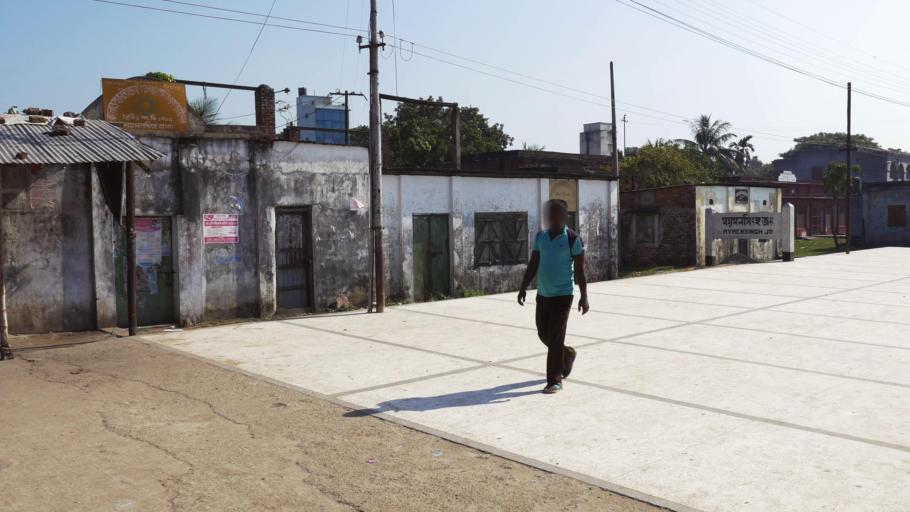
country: BD
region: Dhaka
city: Mymensingh
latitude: 24.6759
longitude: 90.4545
